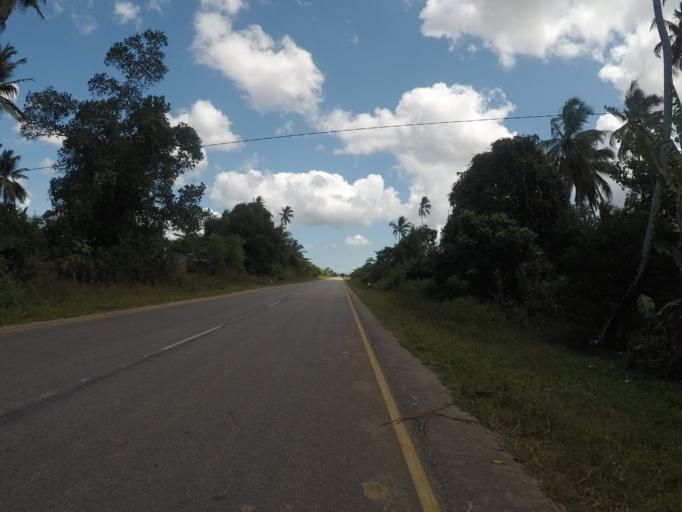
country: TZ
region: Zanzibar Central/South
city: Koani
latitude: -6.1830
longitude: 39.3719
